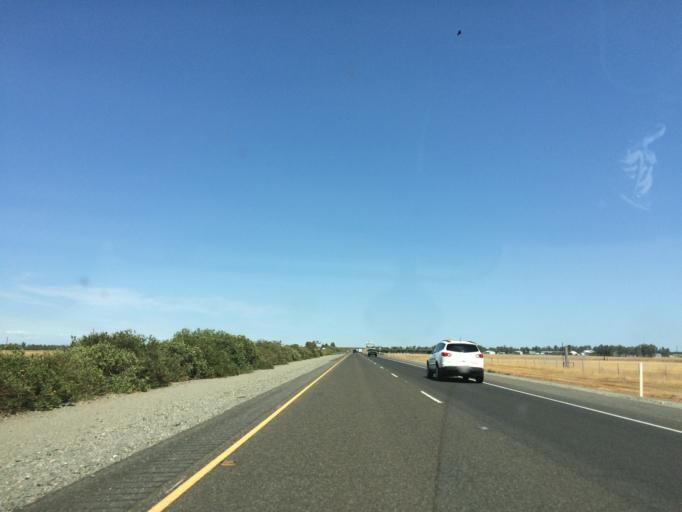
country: US
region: California
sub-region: Glenn County
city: Orland
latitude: 39.6871
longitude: -122.2047
